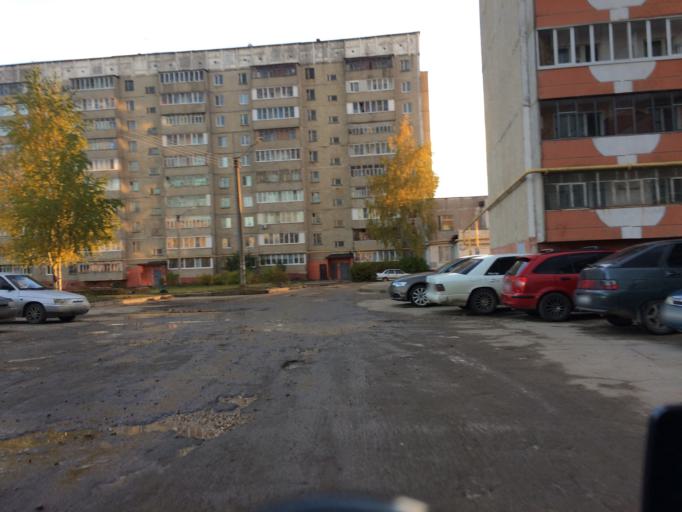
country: RU
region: Mariy-El
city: Yoshkar-Ola
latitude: 56.6356
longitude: 47.9277
